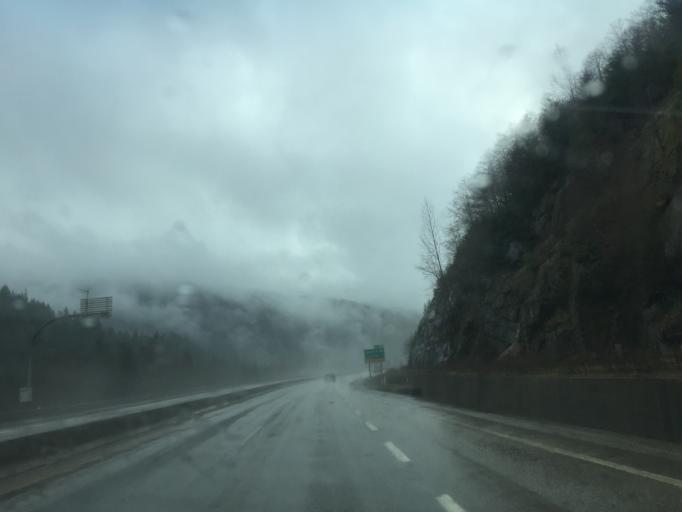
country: CA
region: British Columbia
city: Hope
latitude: 49.5021
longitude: -121.2010
